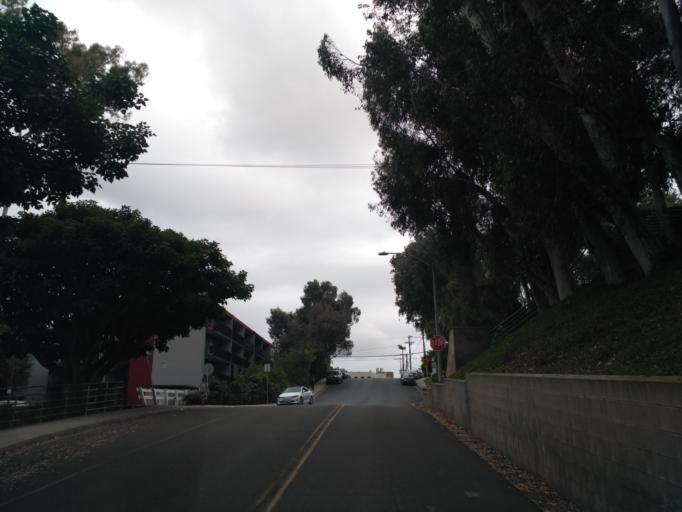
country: US
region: California
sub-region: San Diego County
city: San Diego
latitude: 32.7542
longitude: -117.1633
